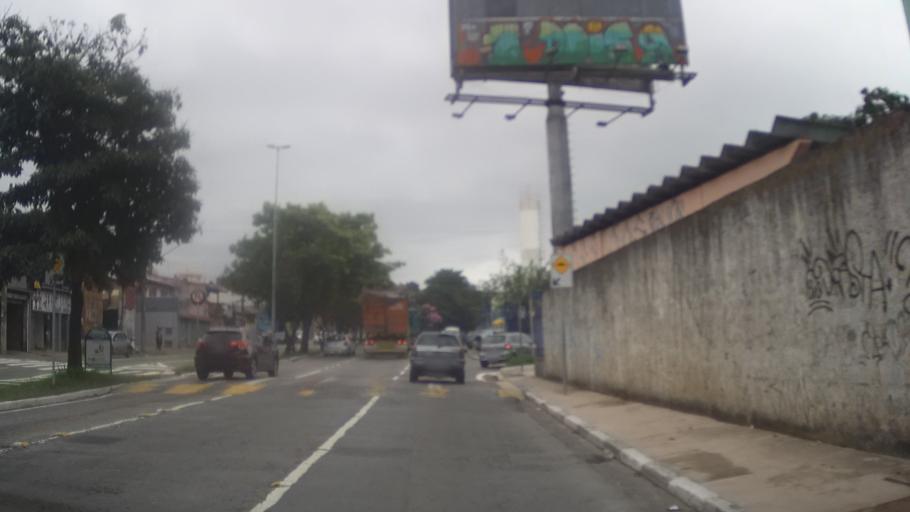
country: BR
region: Sao Paulo
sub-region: Guarulhos
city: Guarulhos
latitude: -23.4373
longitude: -46.5484
